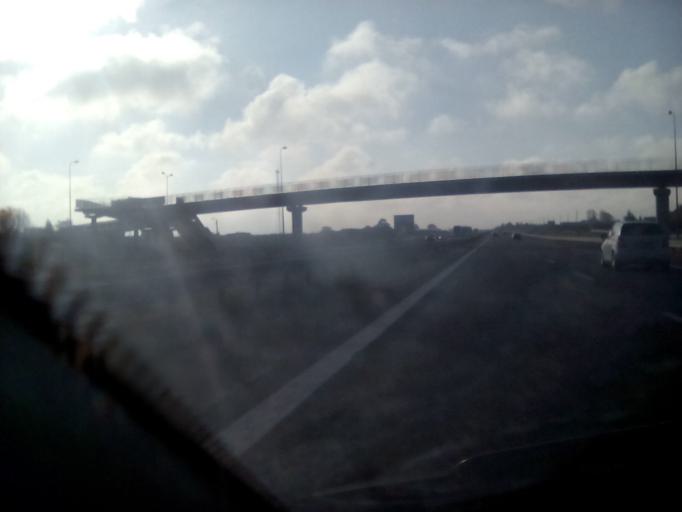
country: PL
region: Masovian Voivodeship
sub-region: Powiat grojecki
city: Jasieniec
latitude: 51.7824
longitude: 20.8953
